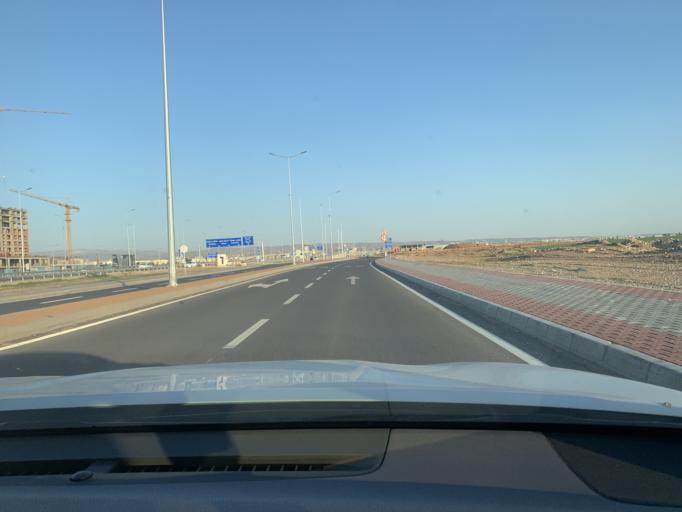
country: IQ
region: Arbil
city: Erbil
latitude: 36.2868
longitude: 44.0389
